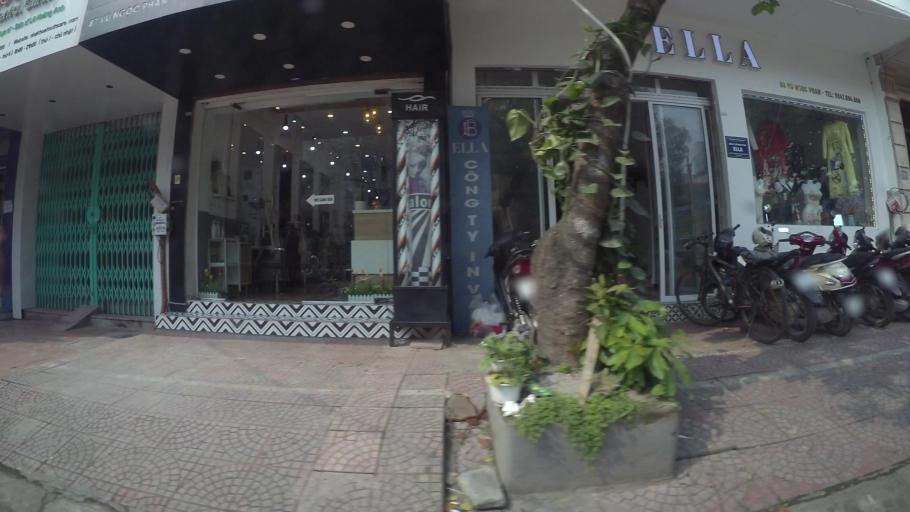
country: VN
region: Ha Noi
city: Cau Giay
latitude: 21.0150
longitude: 105.8093
